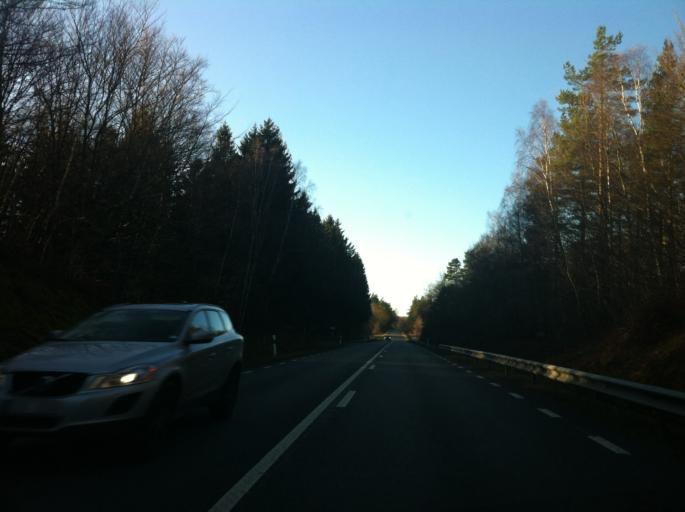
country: SE
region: Blekinge
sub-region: Karlshamns Kommun
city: Morrum
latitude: 56.1706
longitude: 14.6641
